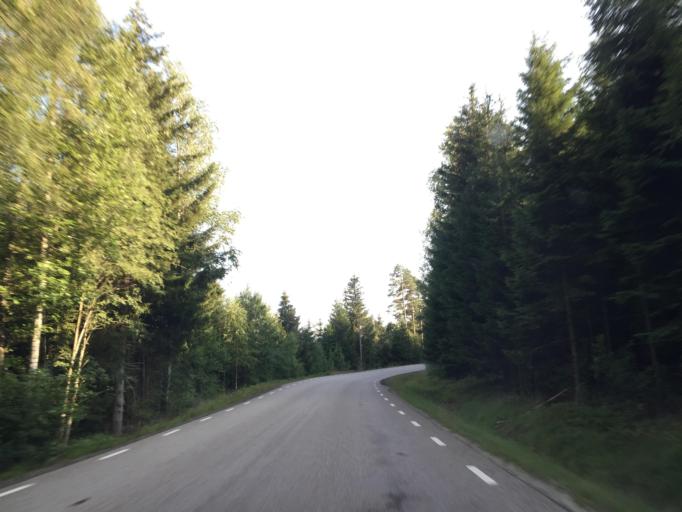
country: SE
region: Vaestra Goetaland
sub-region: Lilla Edets Kommun
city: Lilla Edet
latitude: 58.1360
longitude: 12.0091
